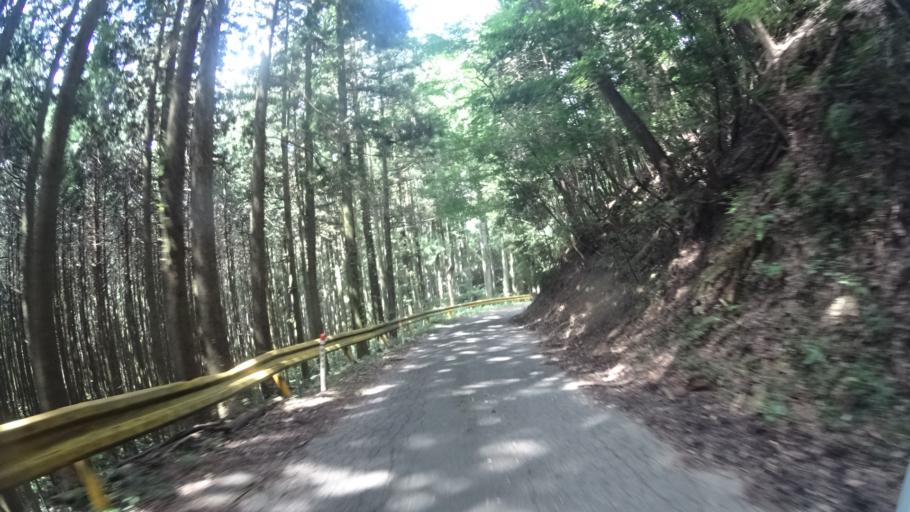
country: JP
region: Yamaguchi
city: Hagi
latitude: 34.4931
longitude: 131.5662
